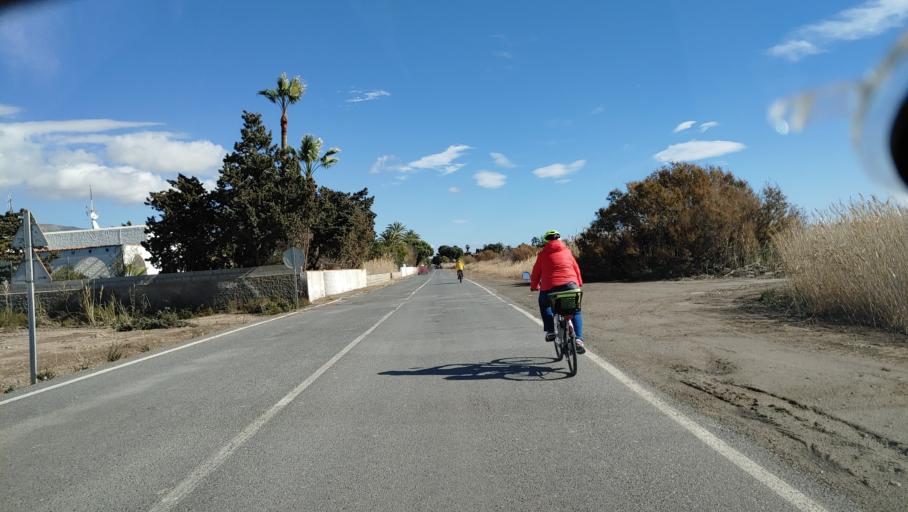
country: ES
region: Andalusia
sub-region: Provincia de Almeria
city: Aguadulce
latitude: 36.7919
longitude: -2.5927
